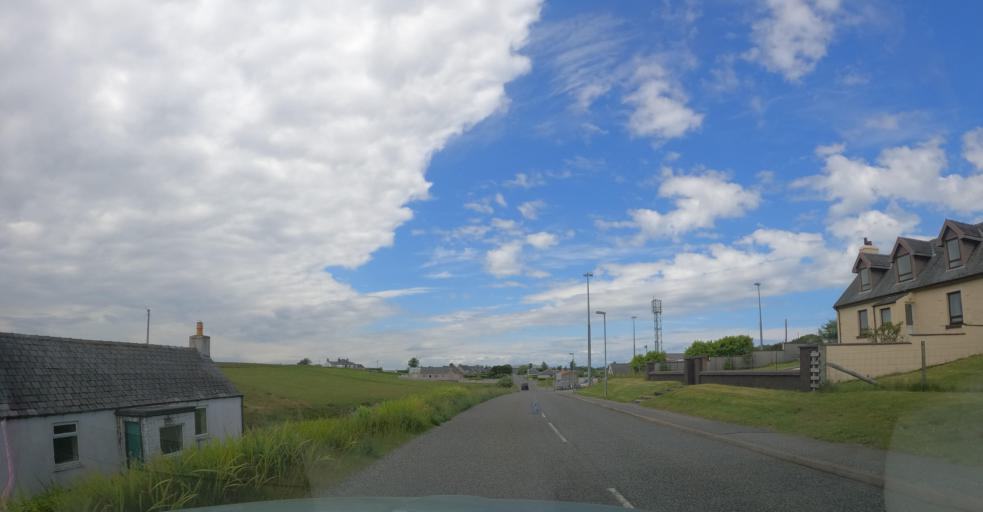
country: GB
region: Scotland
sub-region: Eilean Siar
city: Isle of Lewis
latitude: 58.2753
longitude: -6.3027
